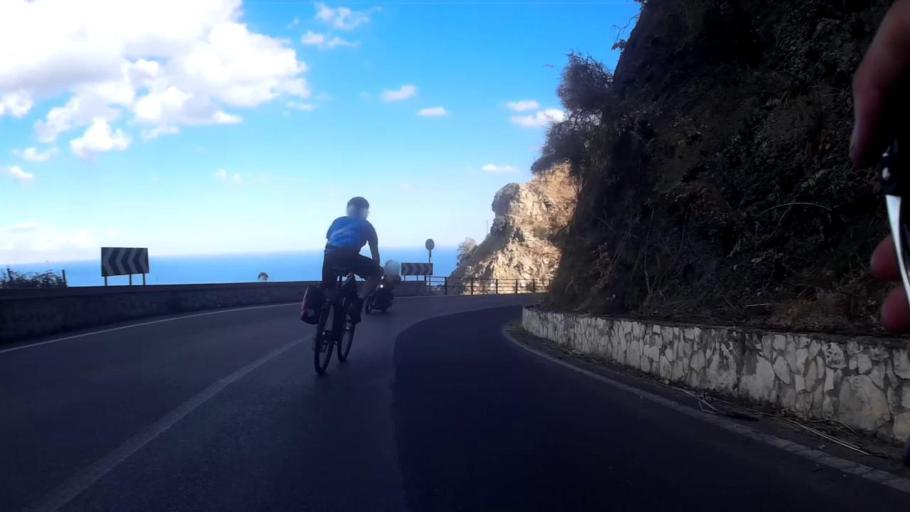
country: IT
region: Sicily
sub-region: Messina
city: Castelmola
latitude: 37.8618
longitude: 15.2791
